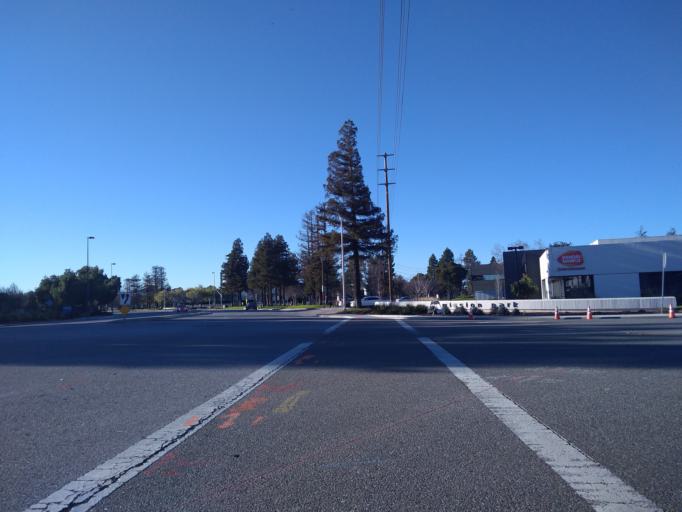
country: US
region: California
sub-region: Santa Clara County
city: Santa Clara
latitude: 37.3879
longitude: -121.9612
